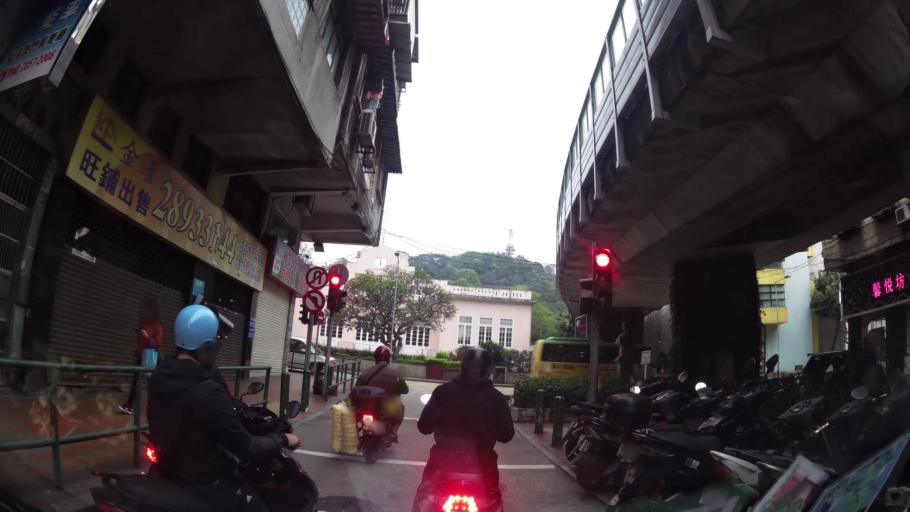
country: MO
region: Macau
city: Macau
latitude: 22.2005
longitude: 113.5499
